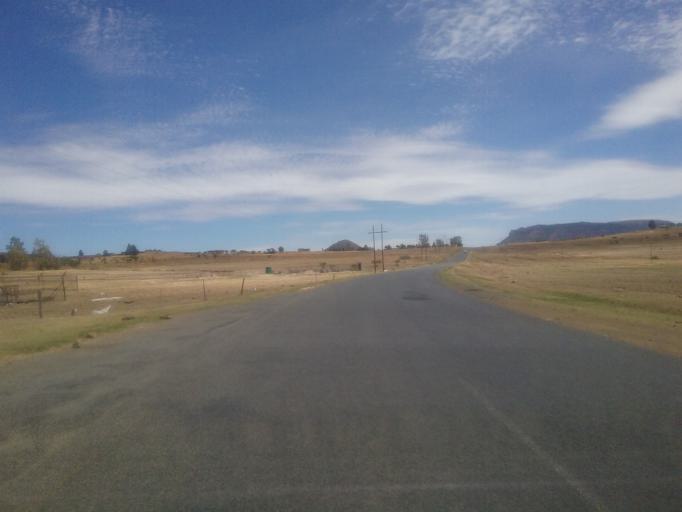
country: LS
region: Mafeteng
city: Mafeteng
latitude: -29.9863
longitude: 27.3270
